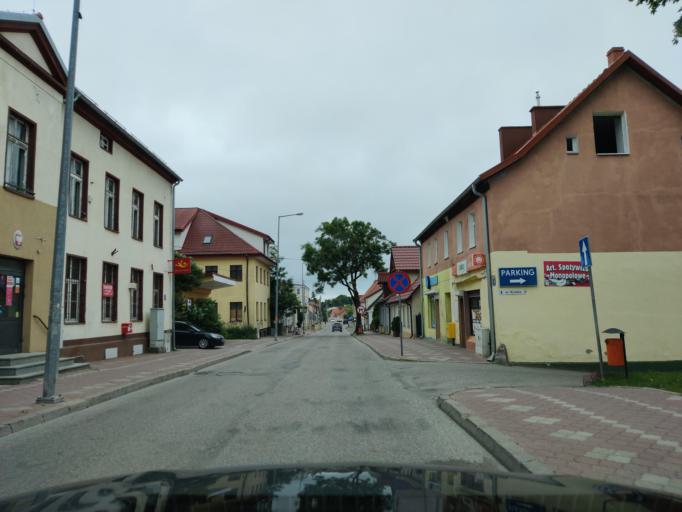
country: PL
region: Warmian-Masurian Voivodeship
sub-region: Powiat gizycki
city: Ryn
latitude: 53.9377
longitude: 21.5465
